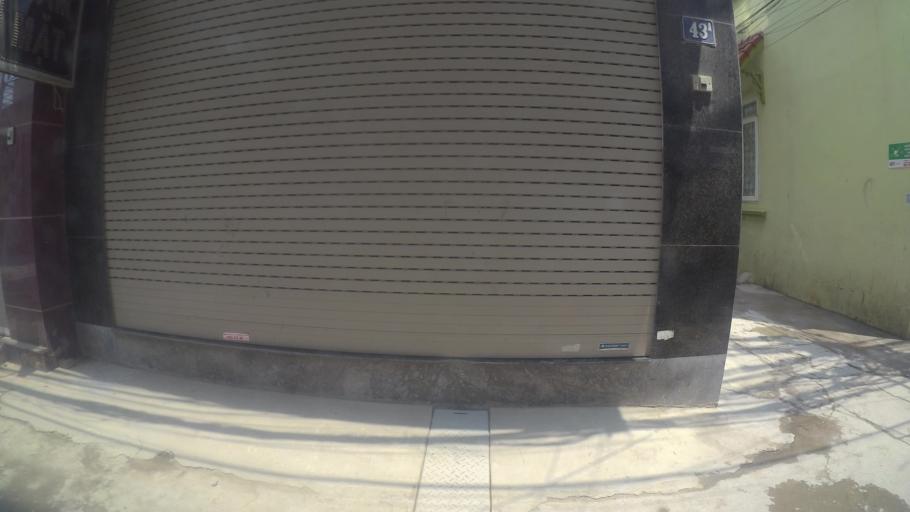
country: VN
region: Ha Noi
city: Tay Ho
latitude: 21.0880
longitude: 105.7874
